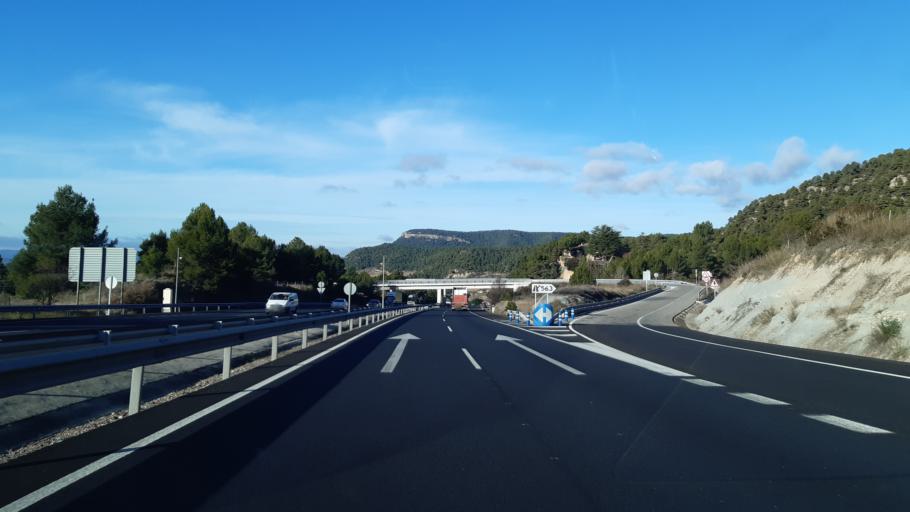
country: ES
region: Catalonia
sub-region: Provincia de Barcelona
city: Castelloli
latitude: 41.5974
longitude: 1.7137
